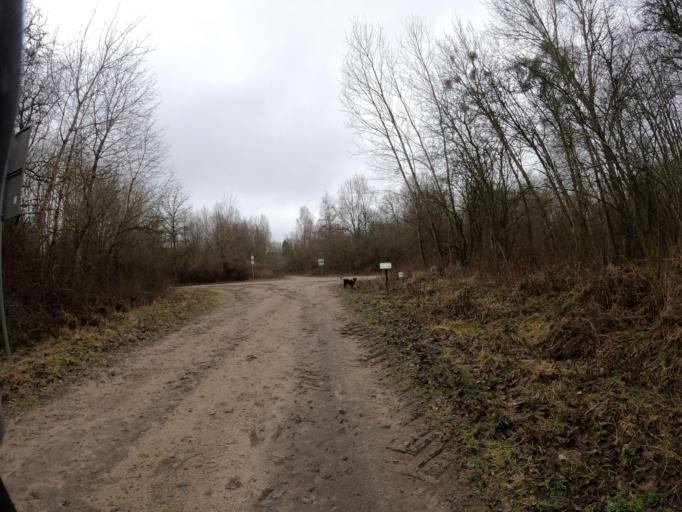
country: PL
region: Greater Poland Voivodeship
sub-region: Powiat zlotowski
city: Sypniewo
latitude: 53.4873
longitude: 16.5648
